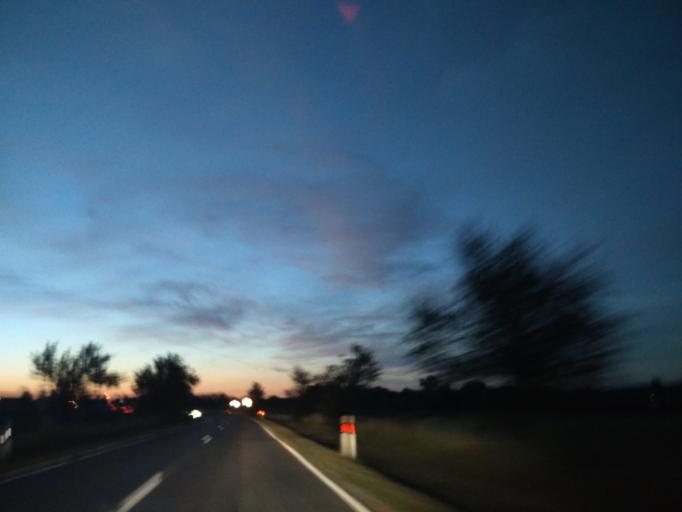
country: HU
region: Zala
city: Zalaegerszeg
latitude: 46.9238
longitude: 16.8588
